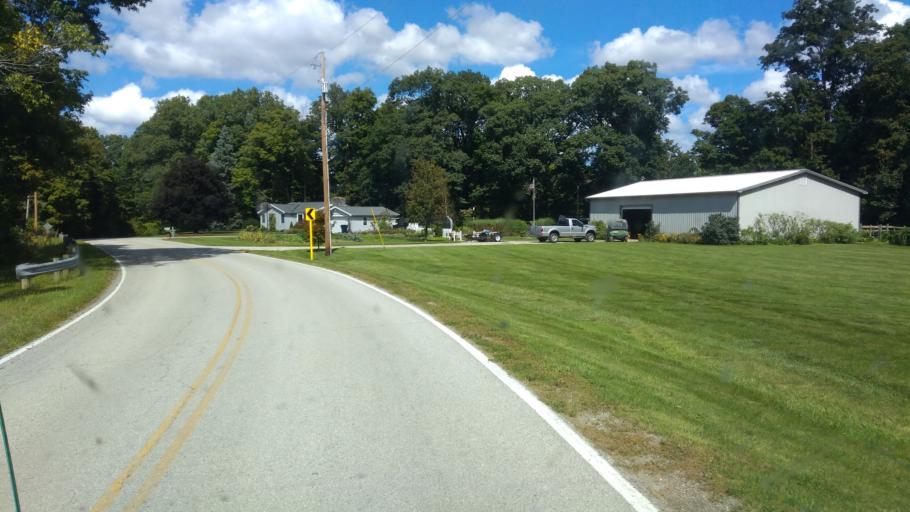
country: US
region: Ohio
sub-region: Huron County
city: Norwalk
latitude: 41.2243
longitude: -82.6511
